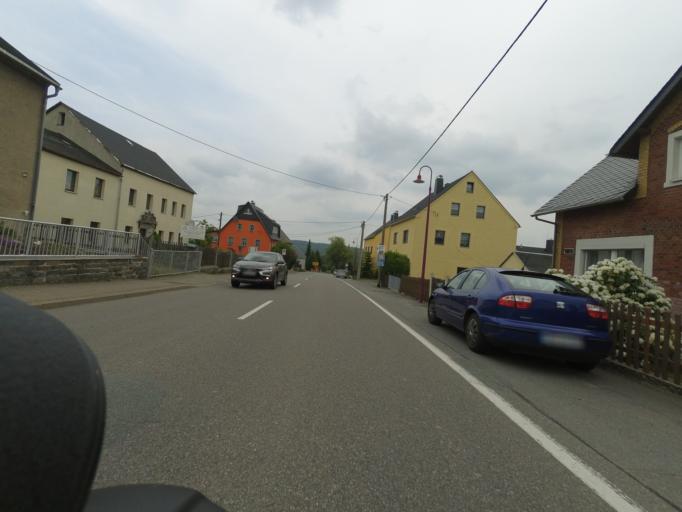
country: DE
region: Saxony
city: Lengefeld
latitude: 50.7408
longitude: 13.1780
